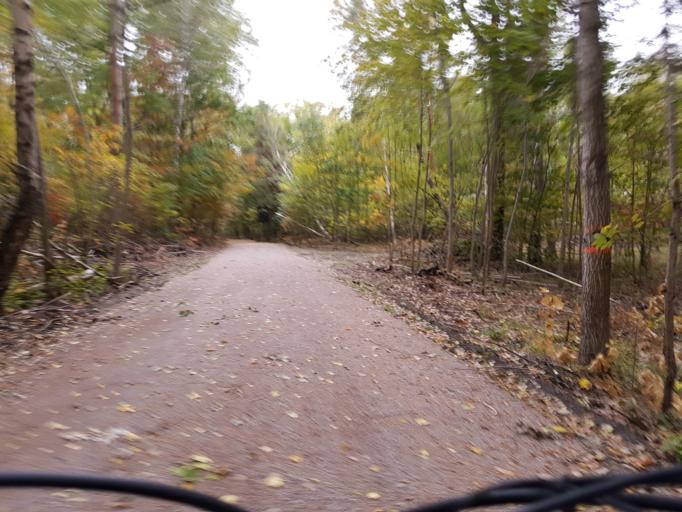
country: DE
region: Brandenburg
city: Trobitz
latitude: 51.5822
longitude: 13.4235
